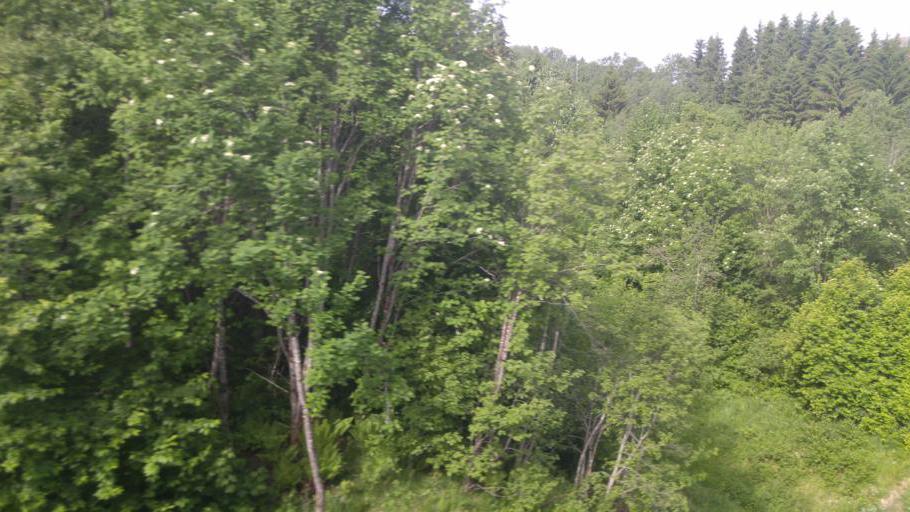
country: NO
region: Sor-Trondelag
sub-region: Trondheim
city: Trondheim
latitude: 63.3809
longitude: 10.3584
